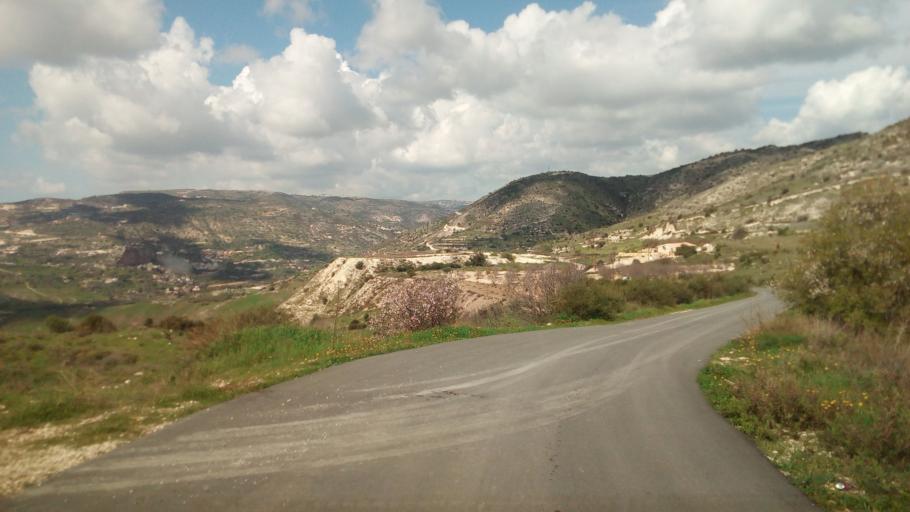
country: CY
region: Pafos
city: Mesogi
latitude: 34.7832
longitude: 32.5473
